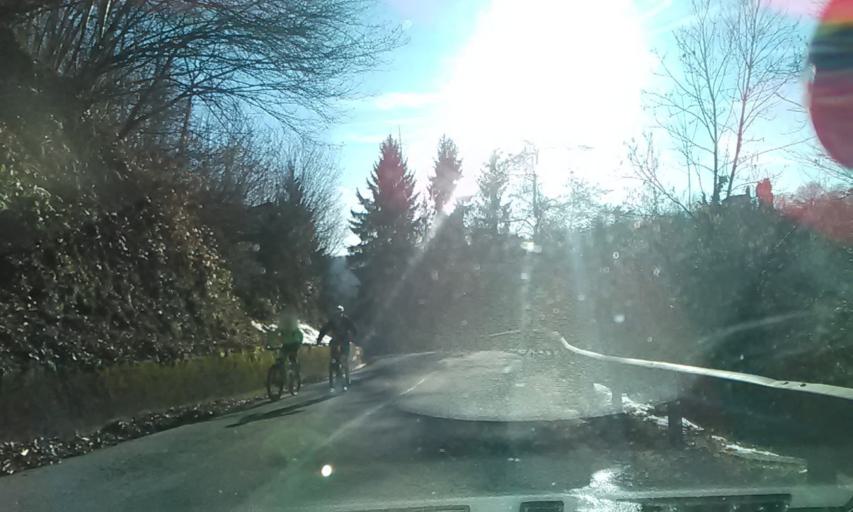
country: IT
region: Piedmont
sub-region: Provincia di Vercelli
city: Valduggia
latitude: 45.7419
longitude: 8.3542
